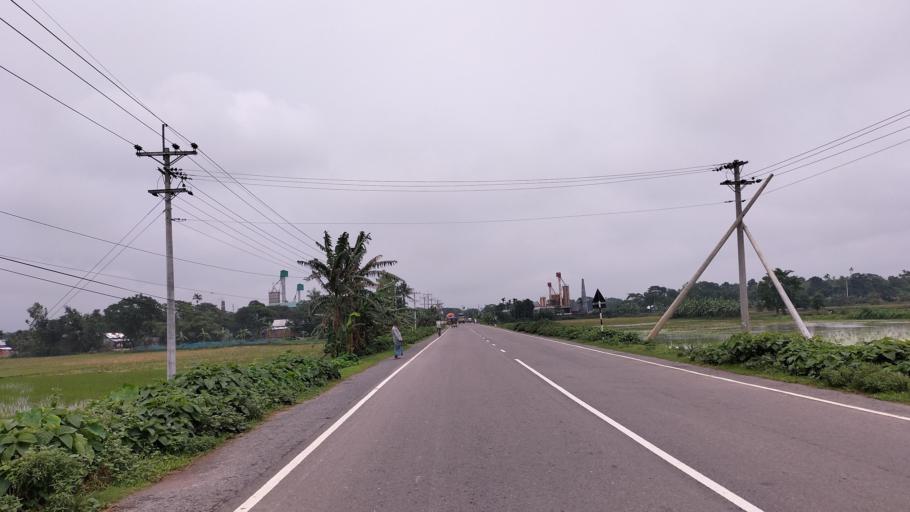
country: BD
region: Dhaka
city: Netrakona
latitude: 24.8526
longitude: 90.6512
